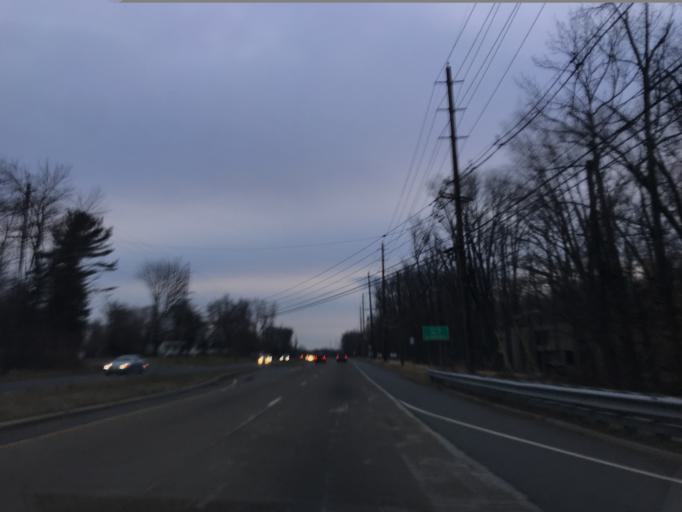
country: US
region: New Jersey
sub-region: Middlesex County
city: Dayton
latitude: 40.4163
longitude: -74.5023
